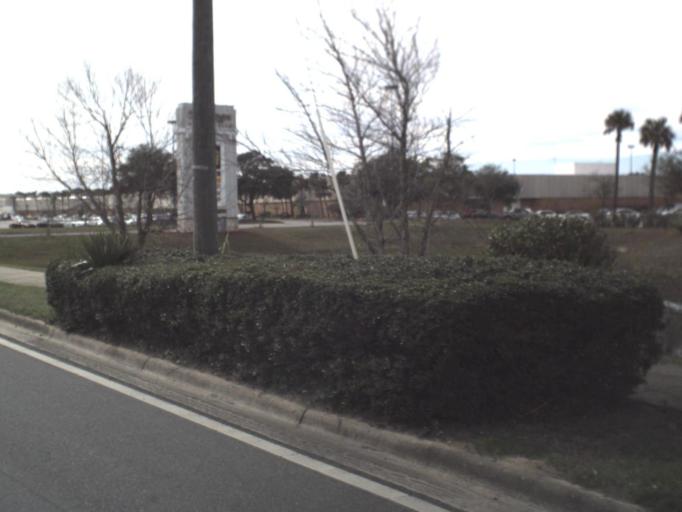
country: US
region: Florida
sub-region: Bay County
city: Hiland Park
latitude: 30.1874
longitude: -85.6439
